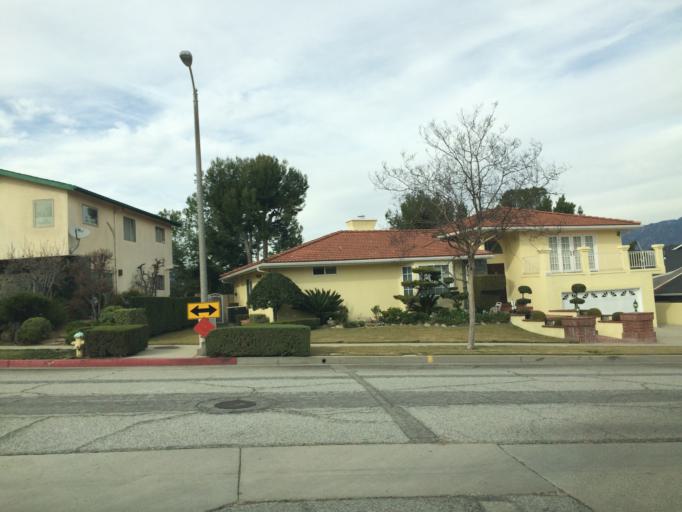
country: US
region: California
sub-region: Los Angeles County
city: South Pasadena
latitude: 34.1021
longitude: -118.1651
